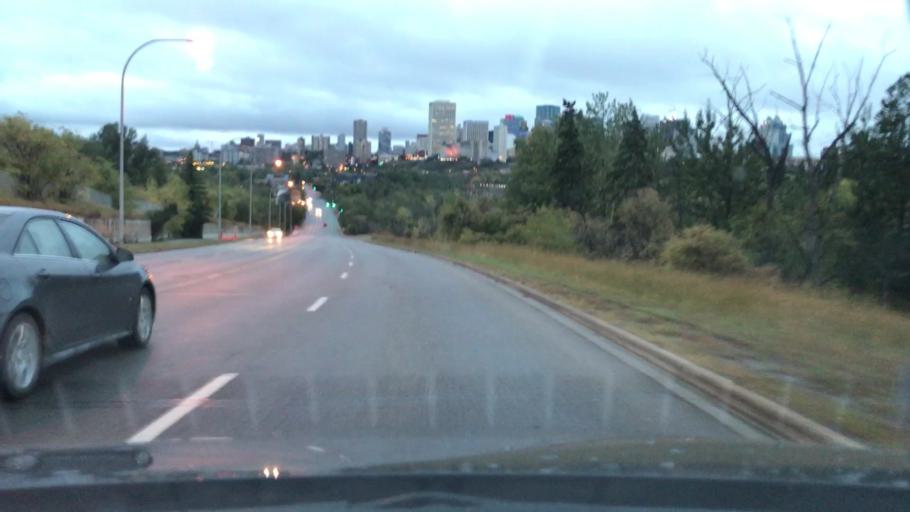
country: CA
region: Alberta
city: Edmonton
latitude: 53.5384
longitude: -113.4615
